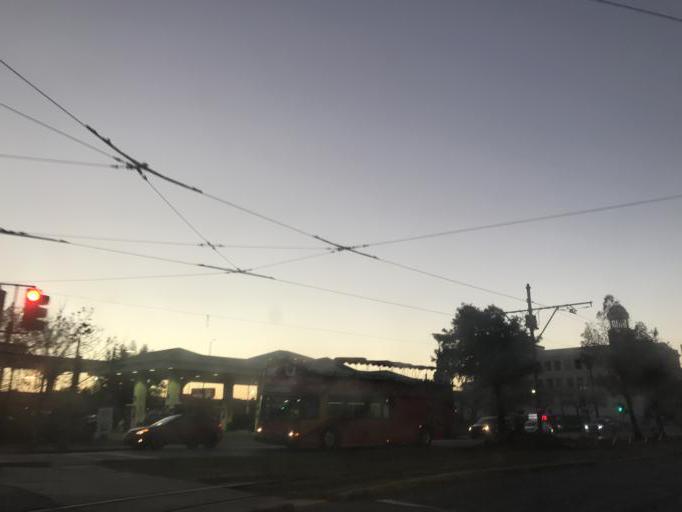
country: US
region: Louisiana
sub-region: Orleans Parish
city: New Orleans
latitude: 29.9437
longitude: -90.0728
